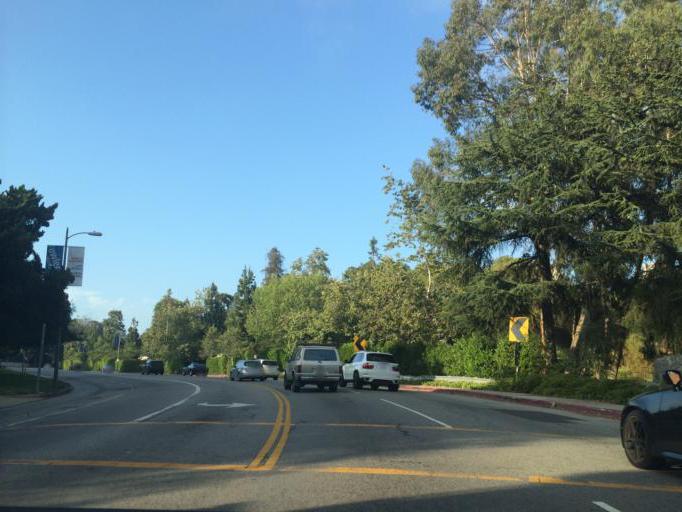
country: US
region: California
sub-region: Los Angeles County
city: Westwood, Los Angeles
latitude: 34.0738
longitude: -118.4452
